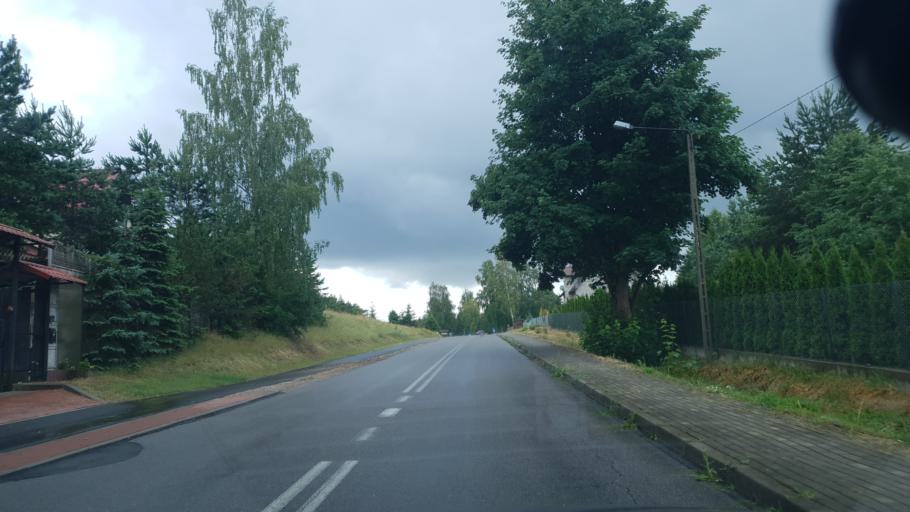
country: PL
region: Pomeranian Voivodeship
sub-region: Powiat kartuski
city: Stezyca
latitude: 54.2340
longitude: 17.9824
